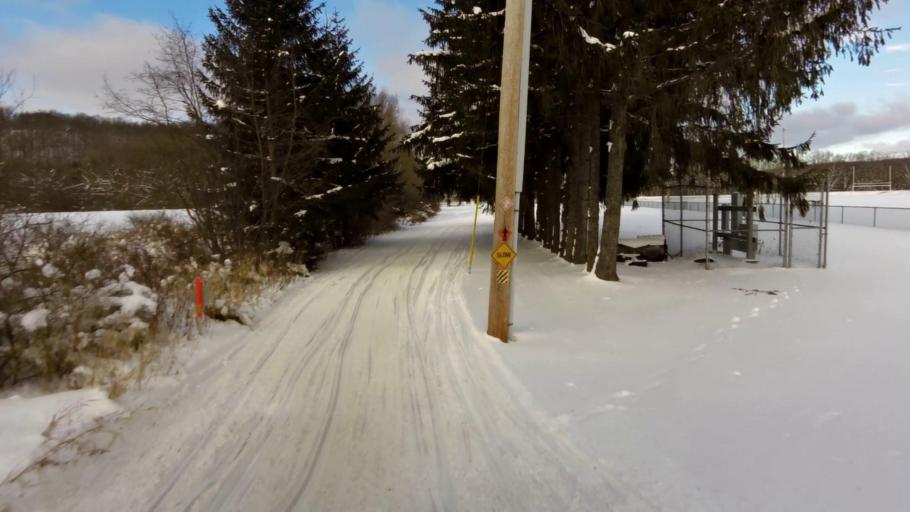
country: US
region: New York
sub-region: Cattaraugus County
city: Franklinville
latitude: 42.3413
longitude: -78.4609
